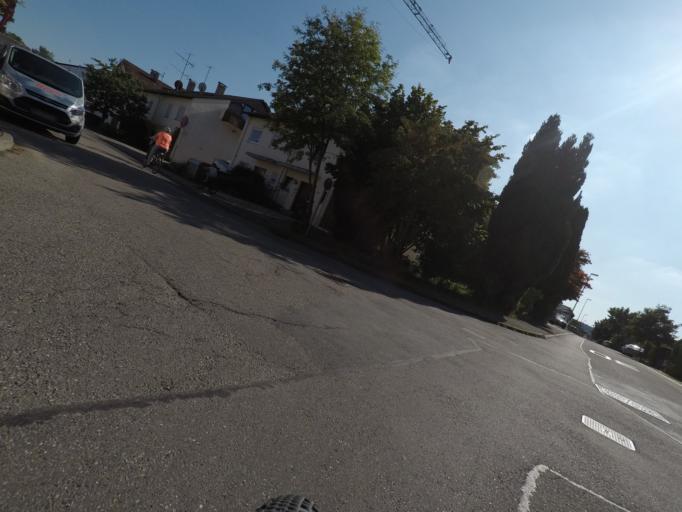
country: DE
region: Baden-Wuerttemberg
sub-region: Regierungsbezirk Stuttgart
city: Hildrizhausen
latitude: 48.6280
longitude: 8.9766
